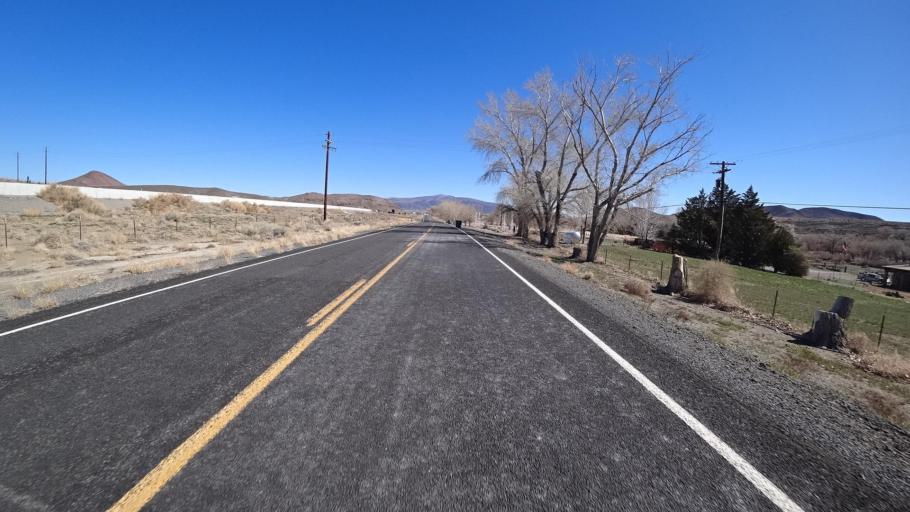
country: US
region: Nevada
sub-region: Lyon County
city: Fernley
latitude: 39.6080
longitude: -119.3215
